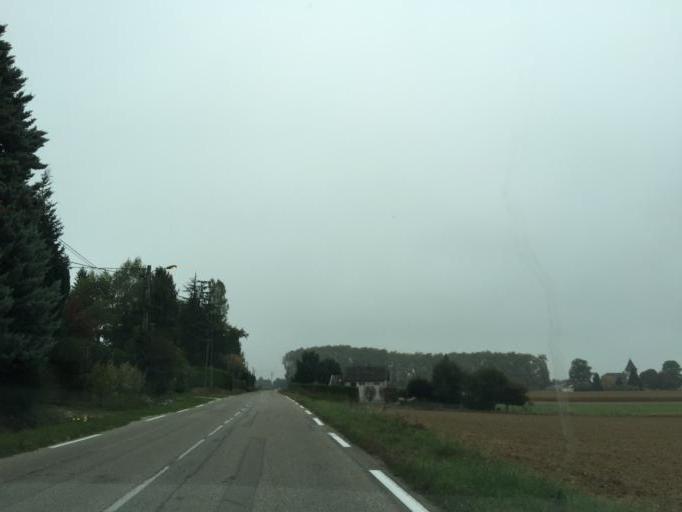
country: FR
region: Rhone-Alpes
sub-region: Departement de l'Isere
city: Saint-Clair-de-la-Tour
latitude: 45.5816
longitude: 5.4935
